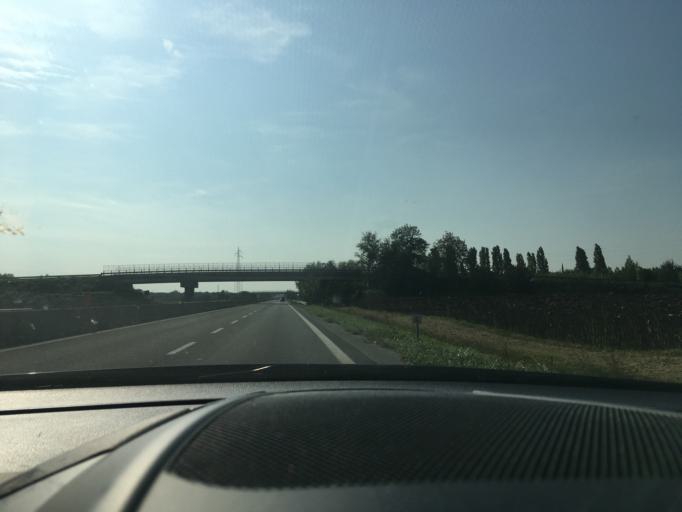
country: IT
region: Emilia-Romagna
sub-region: Provincia di Rimini
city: Bellaria-Igea Marina
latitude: 44.1375
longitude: 12.4612
